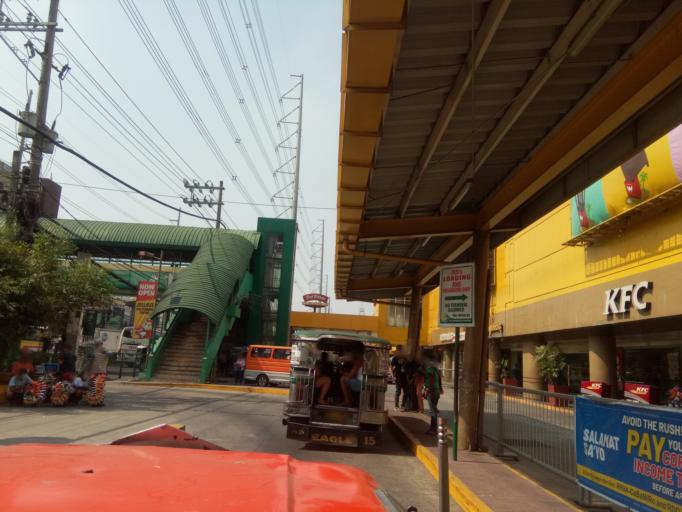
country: PH
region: Calabarzon
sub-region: Province of Cavite
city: Dasmarinas
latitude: 14.3251
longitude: 120.9409
